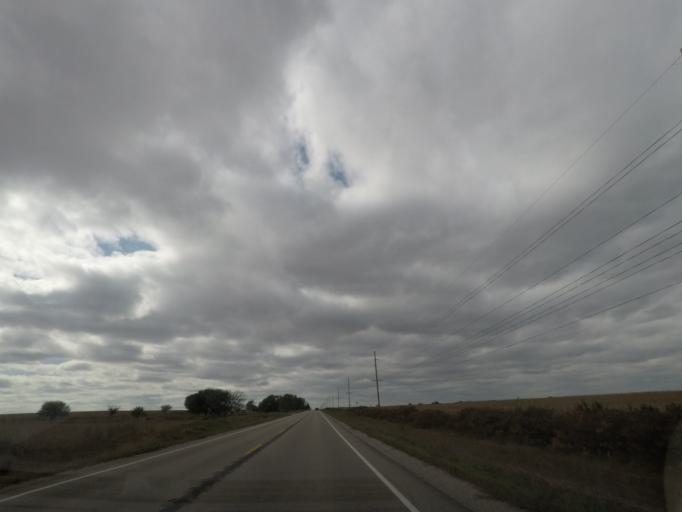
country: US
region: Iowa
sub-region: Story County
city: Huxley
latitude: 41.8778
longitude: -93.5444
